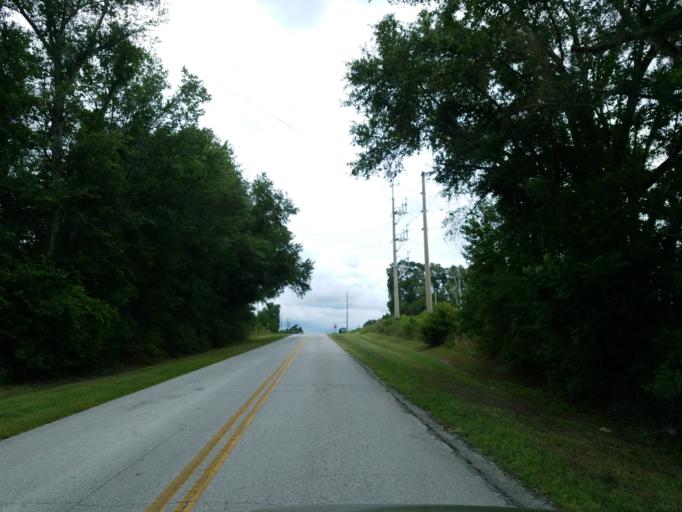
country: US
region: Florida
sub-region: Alachua County
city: High Springs
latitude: 29.9493
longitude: -82.5072
